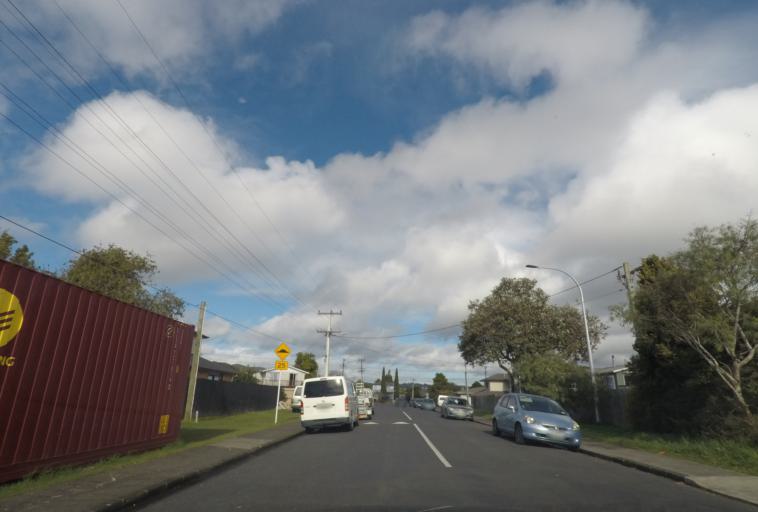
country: NZ
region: Auckland
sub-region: Auckland
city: Waitakere
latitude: -36.8989
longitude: 174.6641
